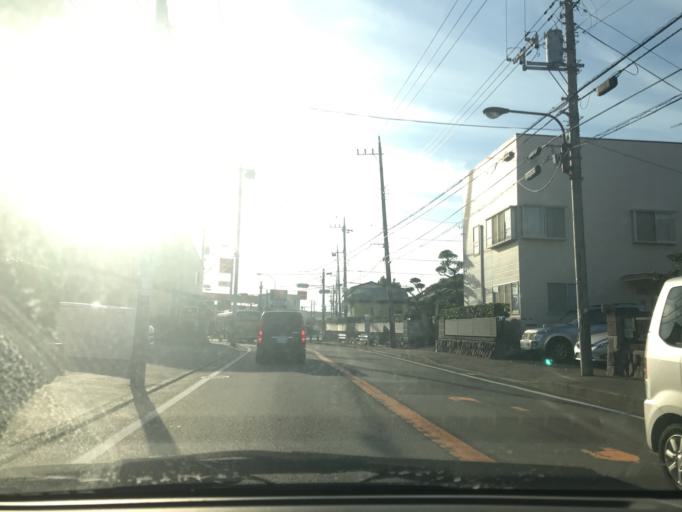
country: JP
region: Kanagawa
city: Fujisawa
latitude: 35.3424
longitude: 139.4716
